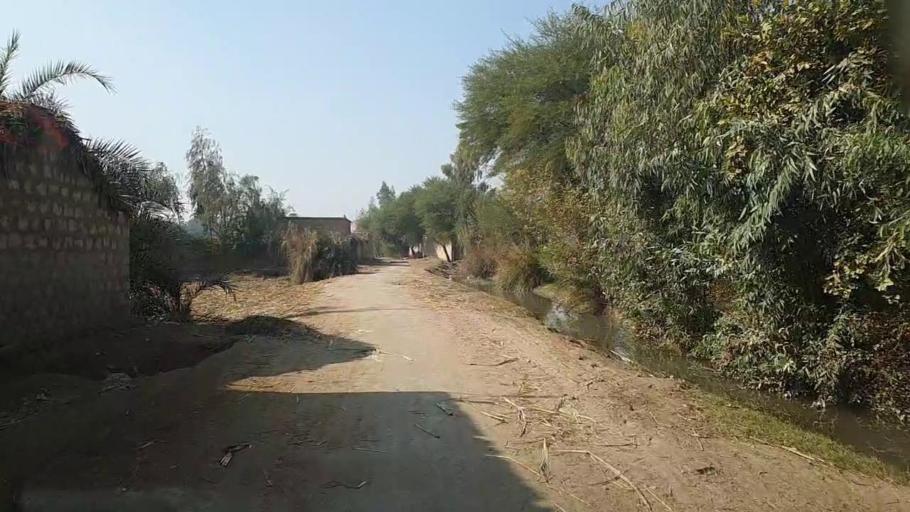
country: PK
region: Sindh
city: Khairpur
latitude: 27.9229
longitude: 69.6609
